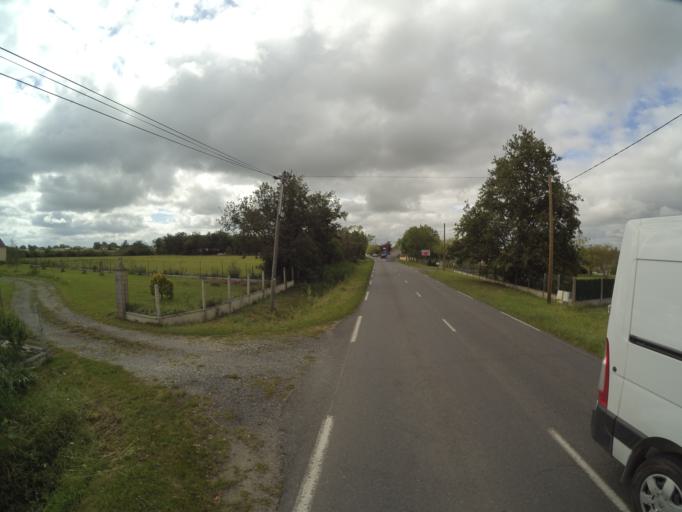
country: FR
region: Aquitaine
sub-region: Departement de la Gironde
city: Macau
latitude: 45.0049
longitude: -0.6067
